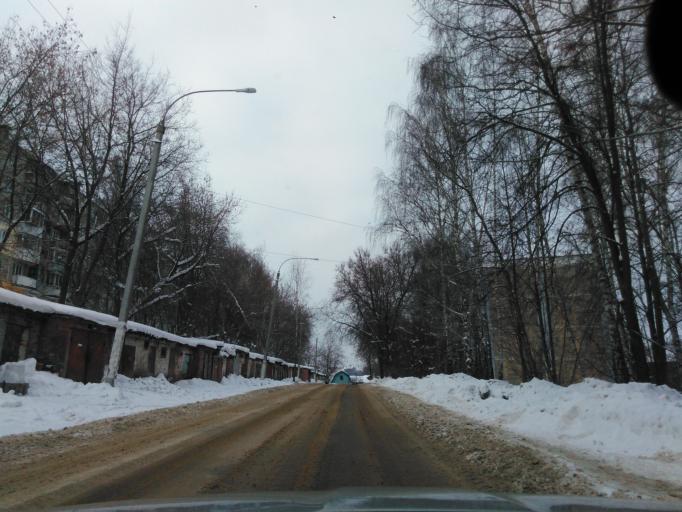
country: RU
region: Moskovskaya
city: Yakhroma
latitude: 56.2828
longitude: 37.4834
